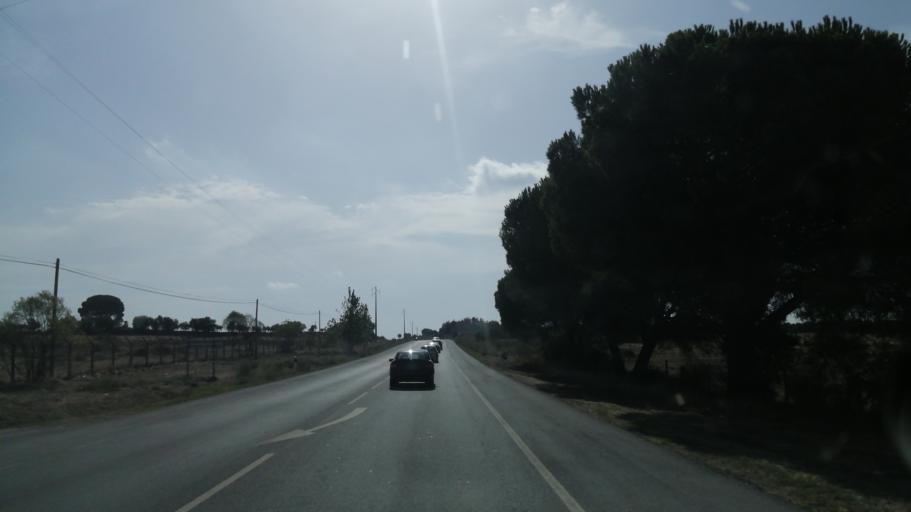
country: PT
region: Evora
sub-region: Evora
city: Evora
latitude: 38.5722
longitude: -7.9806
